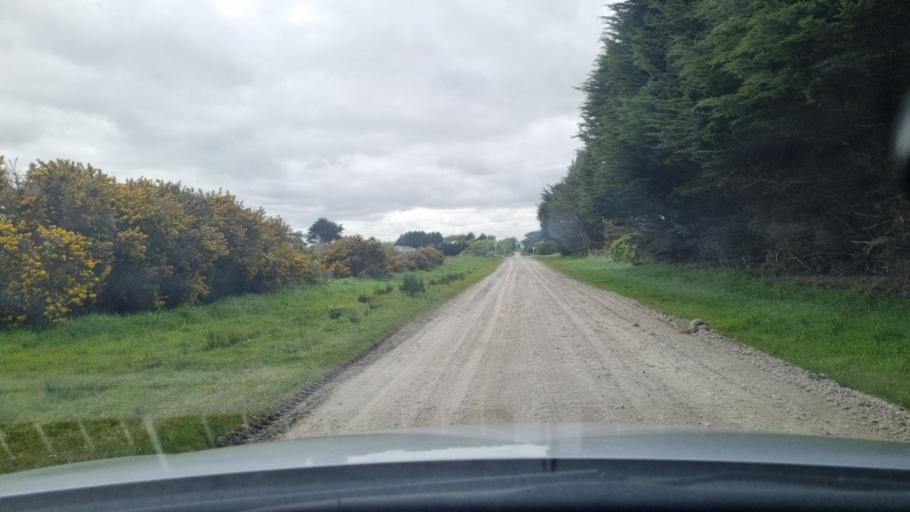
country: NZ
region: Southland
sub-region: Invercargill City
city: Invercargill
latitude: -46.4372
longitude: 168.3896
